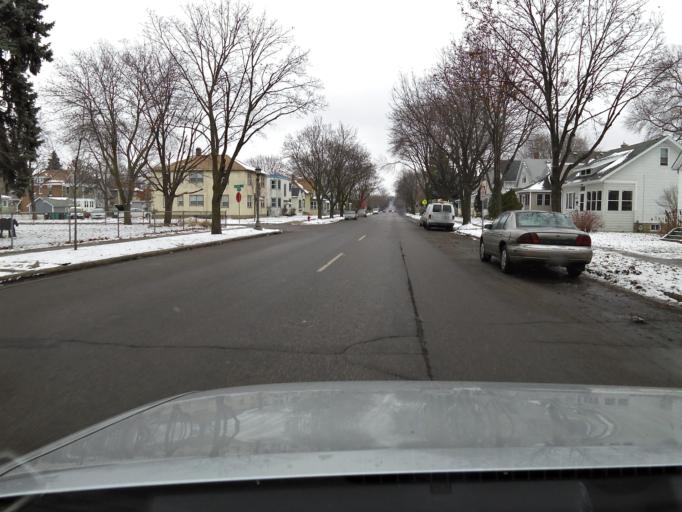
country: US
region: Minnesota
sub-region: Dakota County
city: West Saint Paul
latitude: 44.9269
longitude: -93.1362
